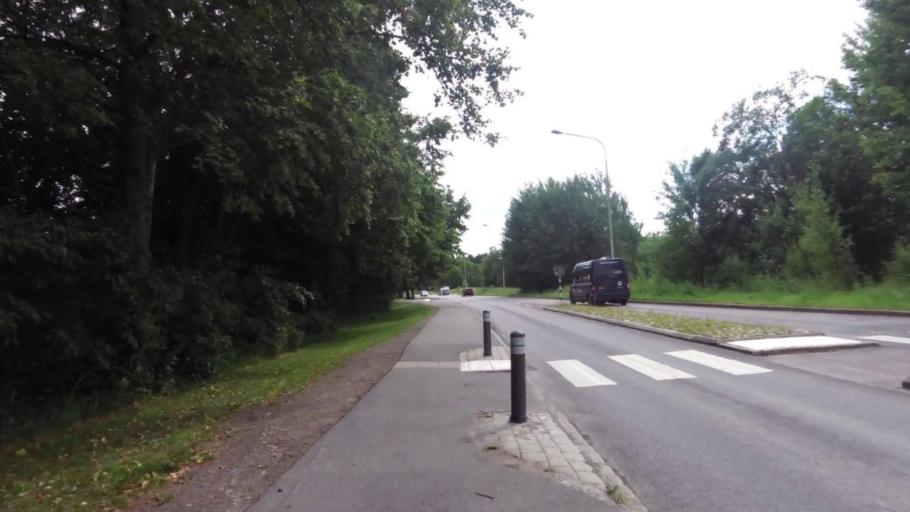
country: SE
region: OEstergoetland
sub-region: Linkopings Kommun
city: Malmslatt
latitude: 58.4091
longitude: 15.5559
